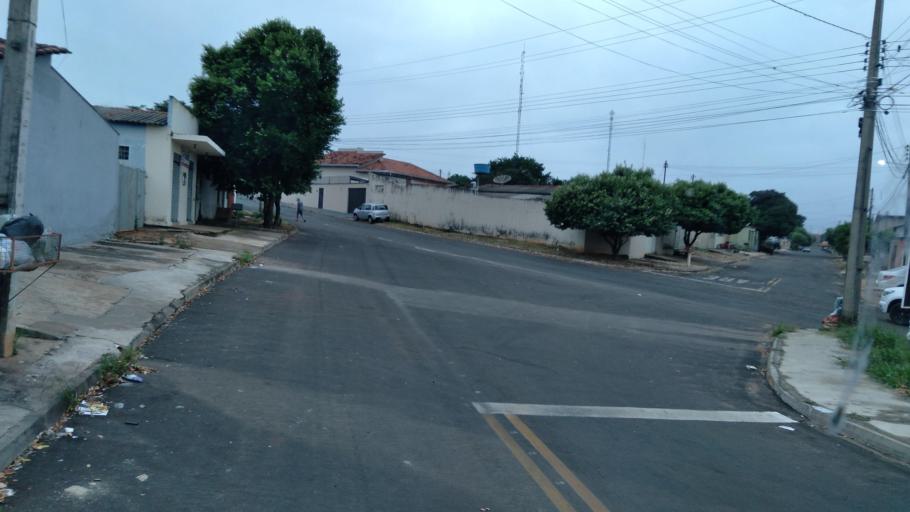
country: BR
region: Goias
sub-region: Mineiros
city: Mineiros
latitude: -17.5754
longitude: -52.5428
